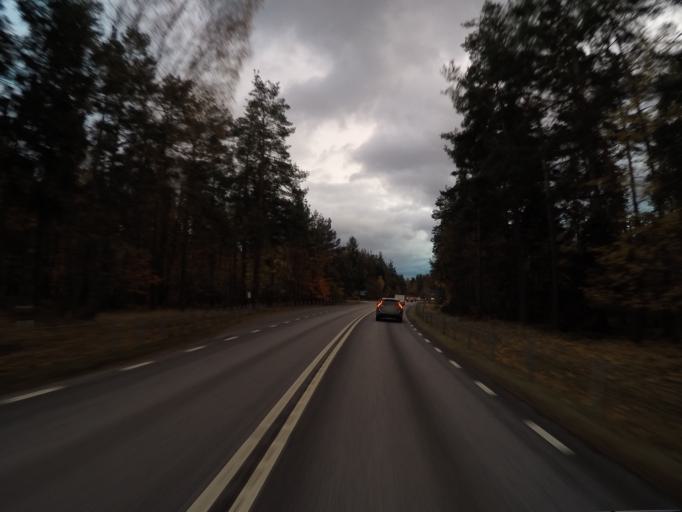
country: SE
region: Skane
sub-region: Kristianstads Kommun
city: Degeberga
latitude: 55.8621
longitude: 14.0910
